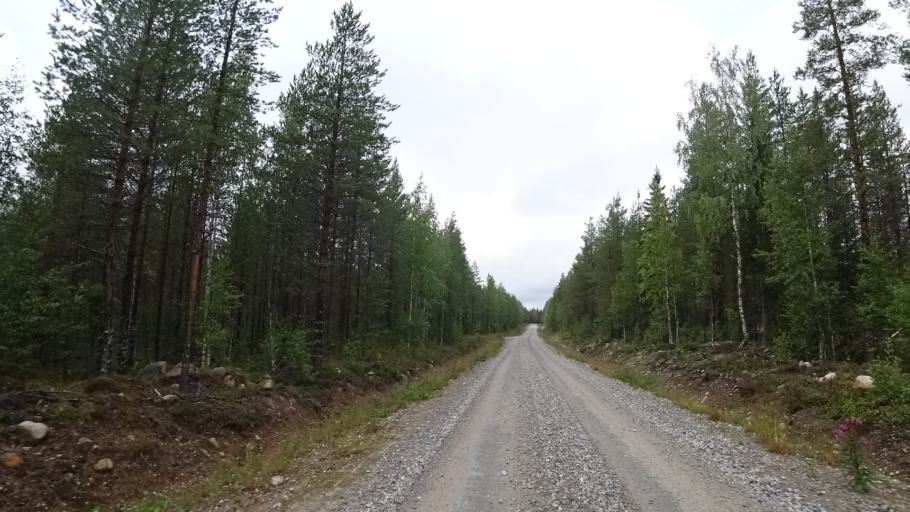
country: FI
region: North Karelia
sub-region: Pielisen Karjala
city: Lieksa
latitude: 63.4677
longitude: 30.2857
